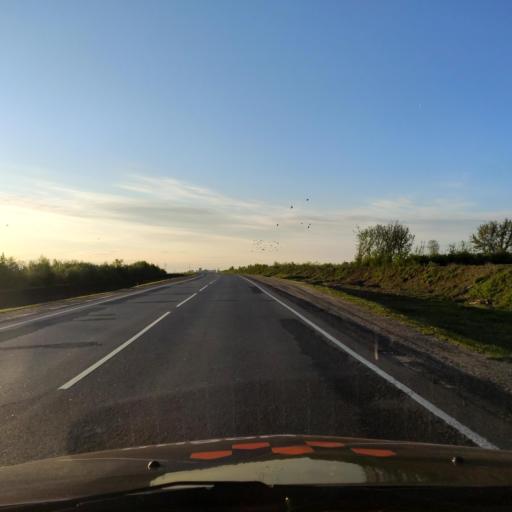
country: RU
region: Orjol
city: Livny
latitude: 52.4418
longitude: 37.5454
